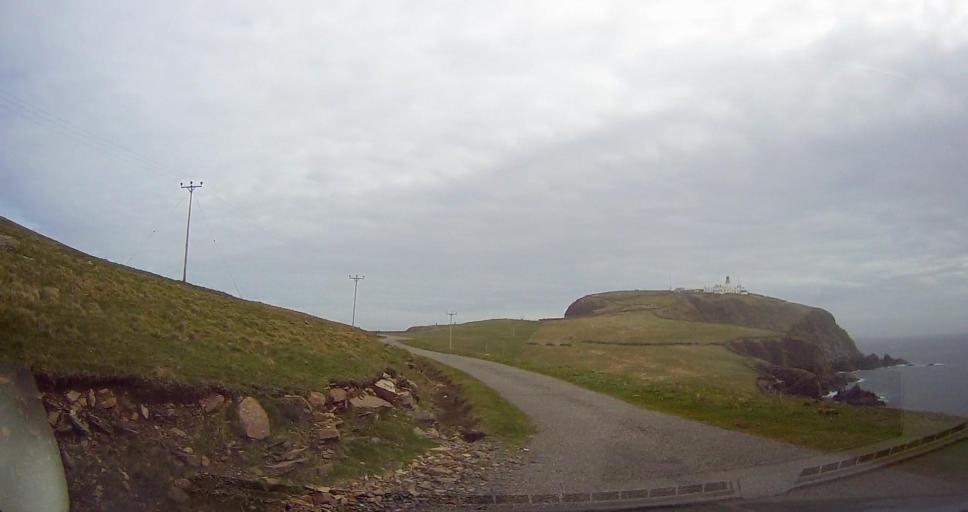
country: GB
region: Scotland
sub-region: Shetland Islands
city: Sandwick
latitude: 59.8597
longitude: -1.2775
